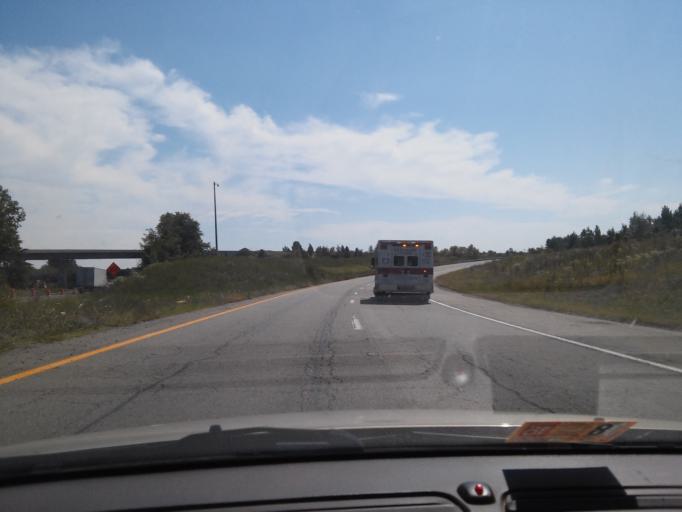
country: US
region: Virginia
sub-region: Henrico County
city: Short Pump
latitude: 37.6740
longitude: -77.6537
